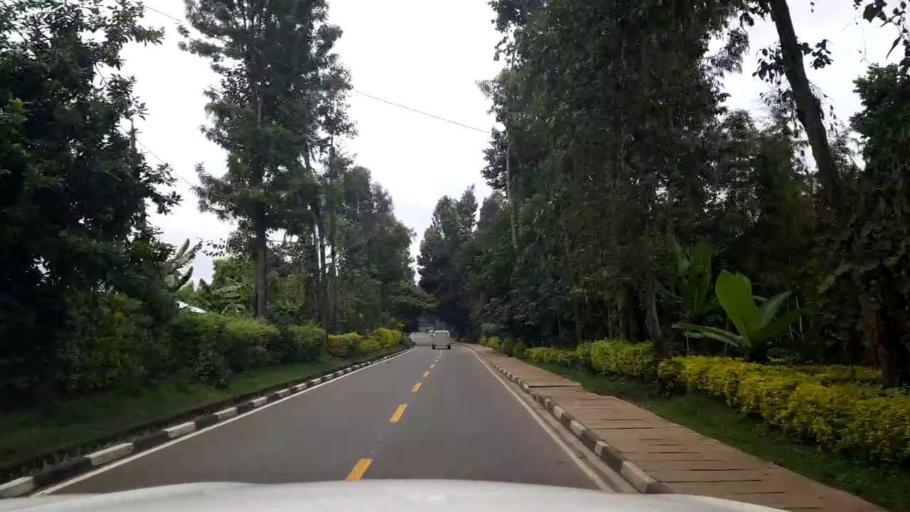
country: RW
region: Northern Province
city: Musanze
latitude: -1.4518
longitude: 29.5964
